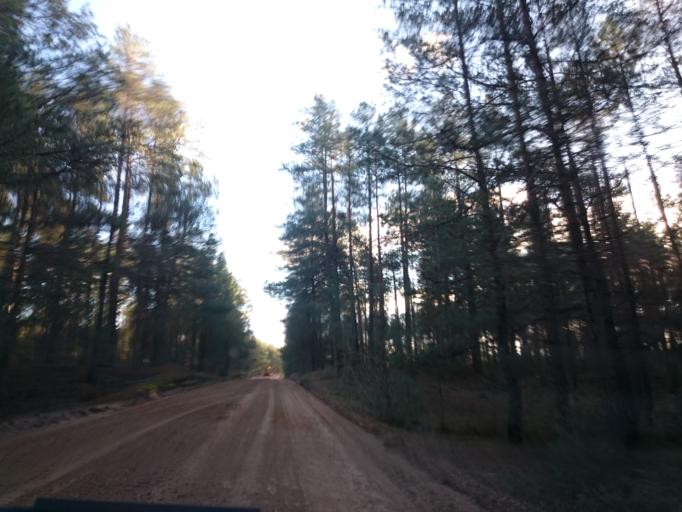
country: LV
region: Garkalne
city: Garkalne
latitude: 57.0607
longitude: 24.4131
